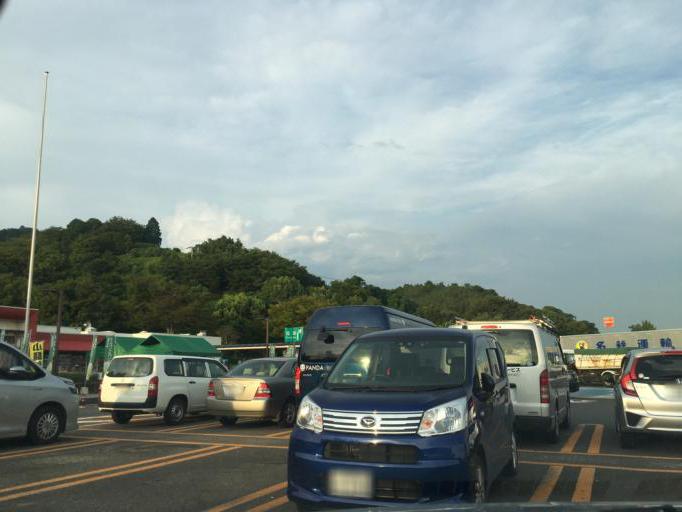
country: JP
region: Saga Prefecture
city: Kanzakimachi-kanzaki
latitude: 33.3297
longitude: 130.3110
